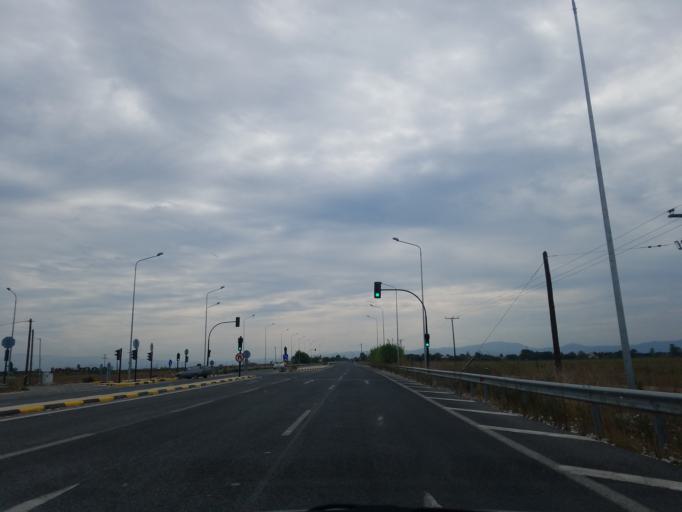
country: GR
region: Thessaly
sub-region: Nomos Kardhitsas
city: Sofades
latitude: 39.3078
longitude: 22.1230
